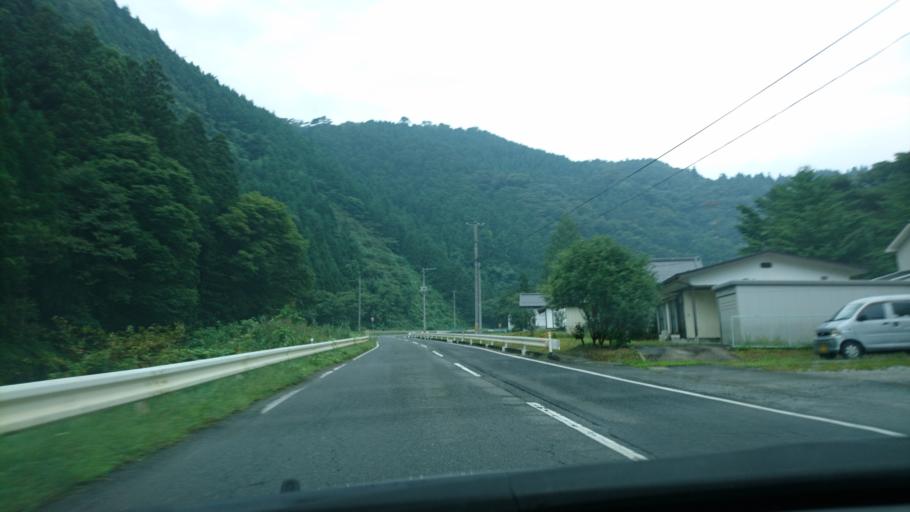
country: JP
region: Iwate
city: Ichinoseki
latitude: 39.0019
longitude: 141.2558
